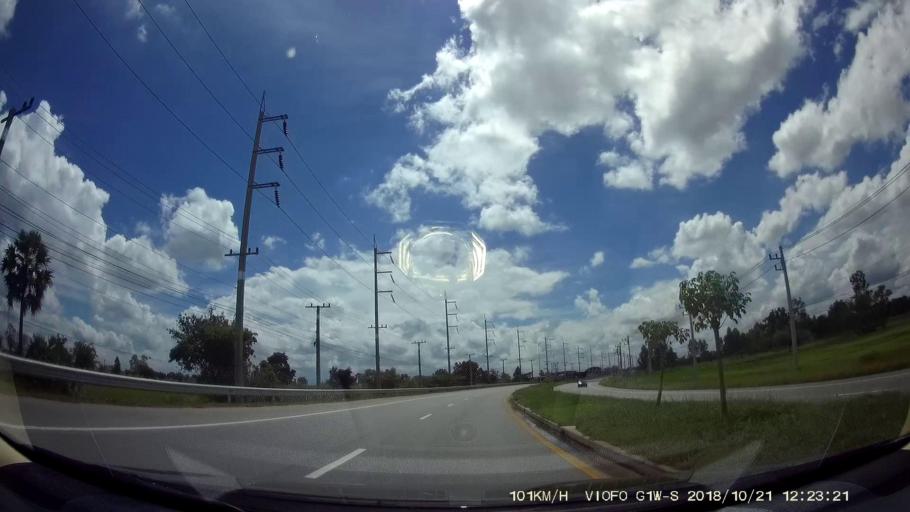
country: TH
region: Nakhon Ratchasima
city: Dan Khun Thot
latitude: 15.2467
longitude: 101.7884
